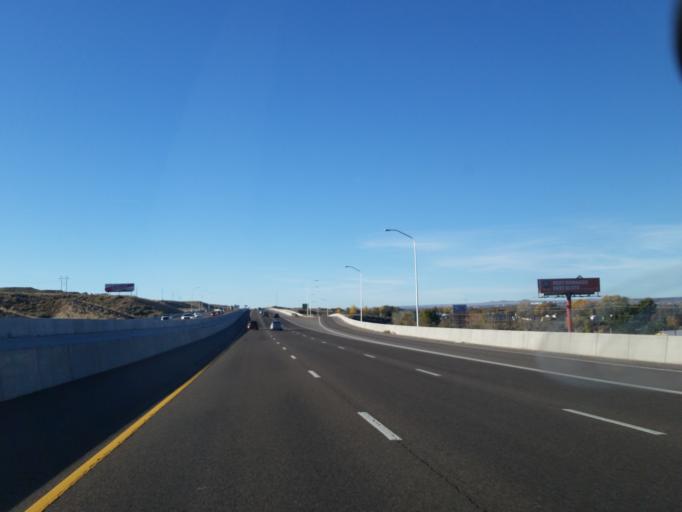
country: US
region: New Mexico
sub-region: Sandoval County
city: Bernalillo
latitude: 35.2998
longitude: -106.5400
